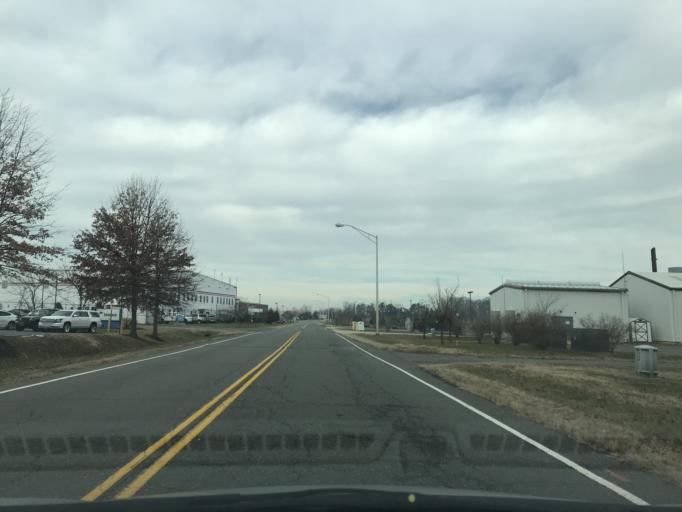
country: US
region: Virginia
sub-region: City of Manassas
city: Manassas
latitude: 38.7305
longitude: -77.5137
